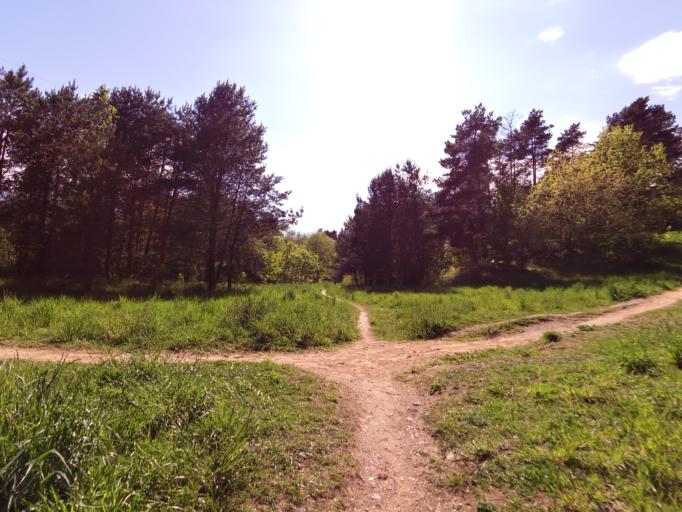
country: LT
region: Vilnius County
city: Seskine
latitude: 54.7213
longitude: 25.2628
